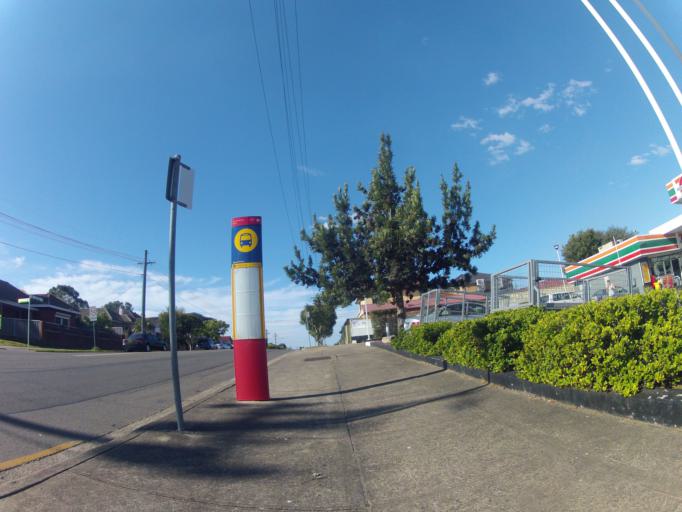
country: AU
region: New South Wales
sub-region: Hurstville
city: Penshurst
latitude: -33.9615
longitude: 151.0791
